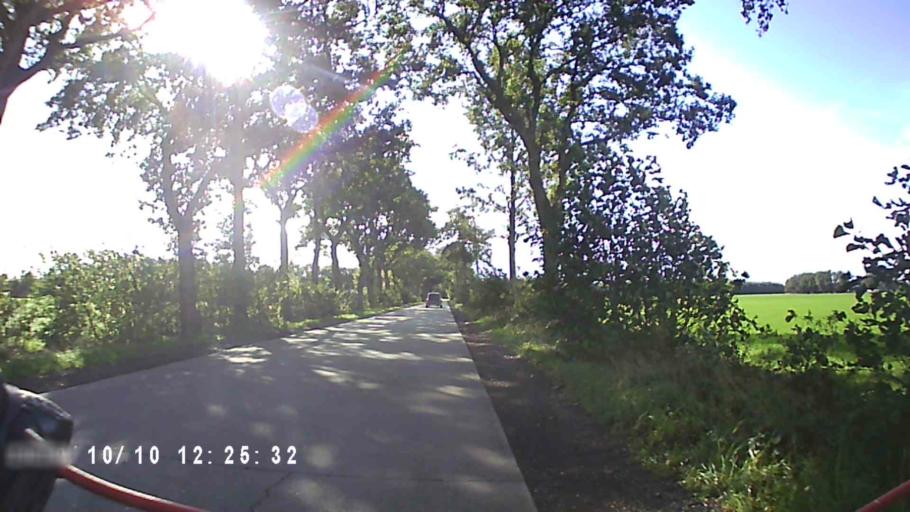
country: NL
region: Friesland
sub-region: Gemeente Heerenveen
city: Jubbega
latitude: 52.9886
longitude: 6.1799
